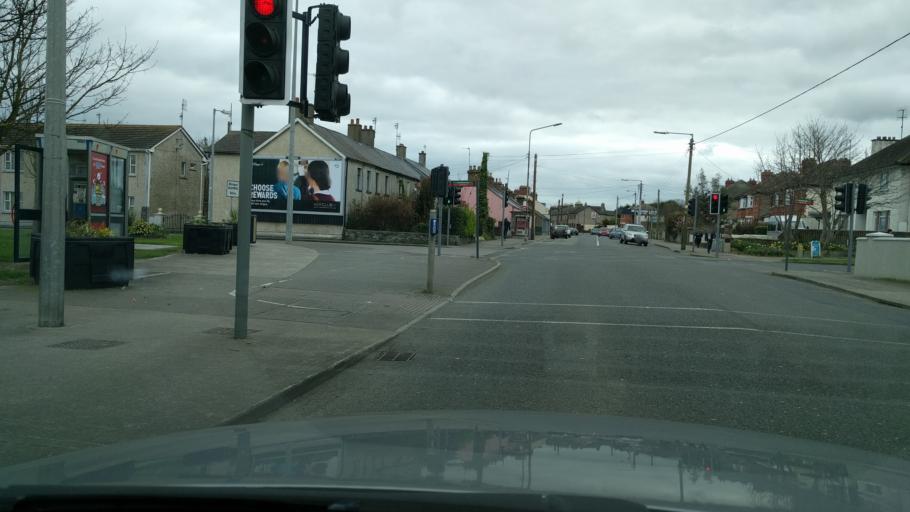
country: IE
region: Leinster
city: Balbriggan
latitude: 53.6135
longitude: -6.1892
